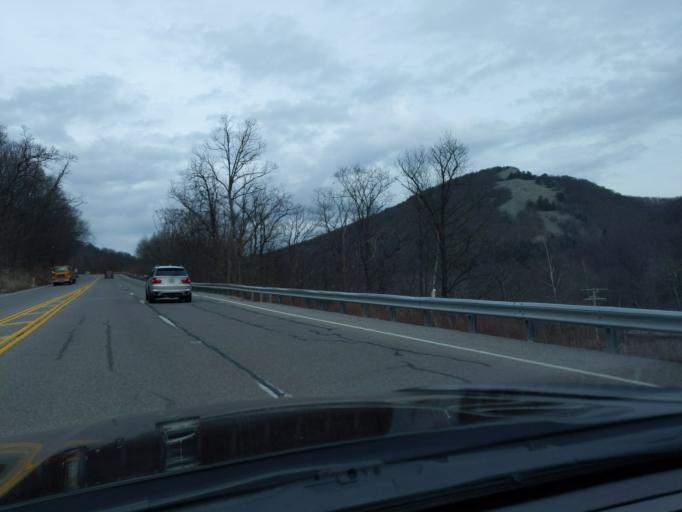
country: US
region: Pennsylvania
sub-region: Blair County
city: Williamsburg
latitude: 40.4859
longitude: -78.2476
